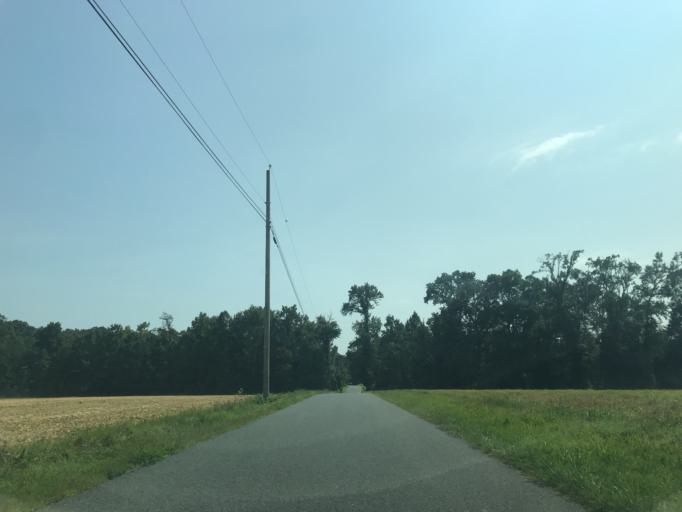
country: US
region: Maryland
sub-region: Baltimore County
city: Bowleys Quarters
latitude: 39.3694
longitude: -76.3794
